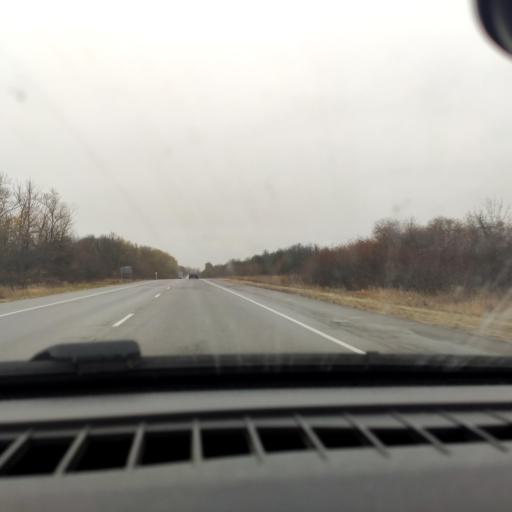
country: RU
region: Voronezj
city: Kolodeznyy
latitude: 51.2778
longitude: 39.0451
